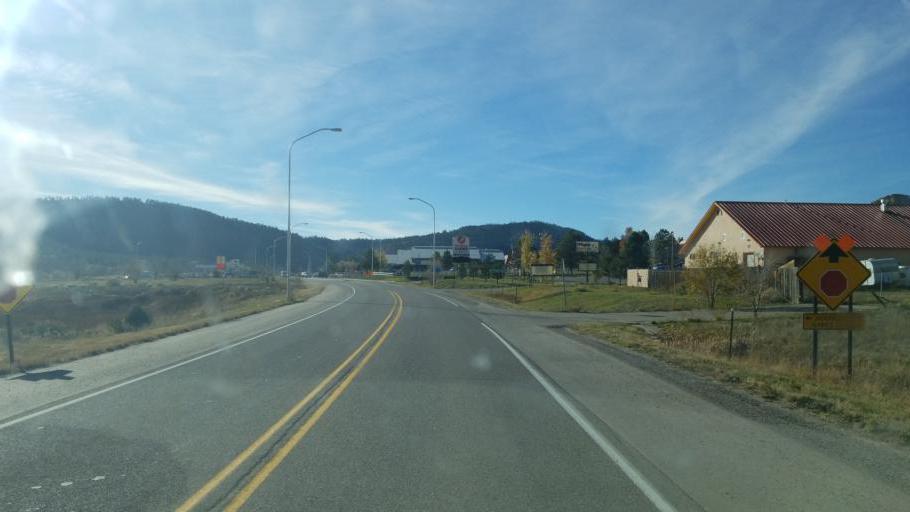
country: US
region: New Mexico
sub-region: Rio Arriba County
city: Dulce
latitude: 36.9343
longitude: -106.9848
